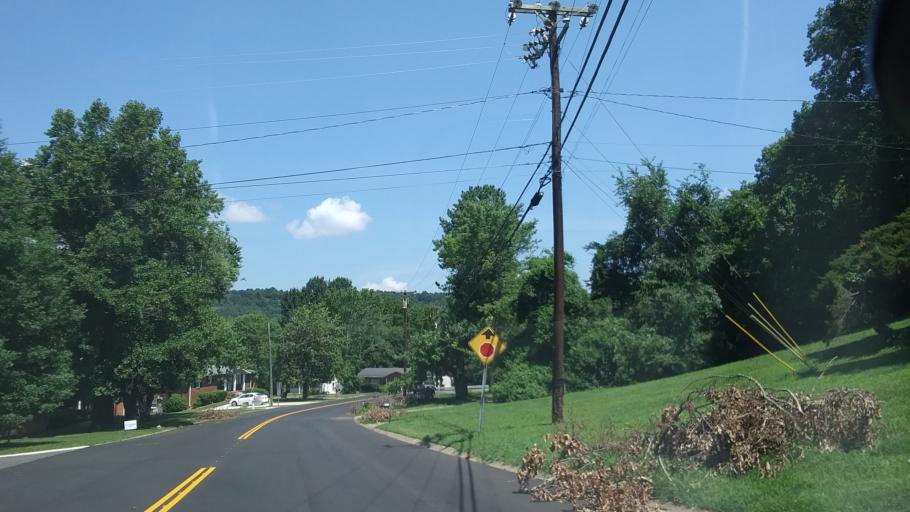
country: US
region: Tennessee
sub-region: Davidson County
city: Belle Meade
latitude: 36.0839
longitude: -86.9389
